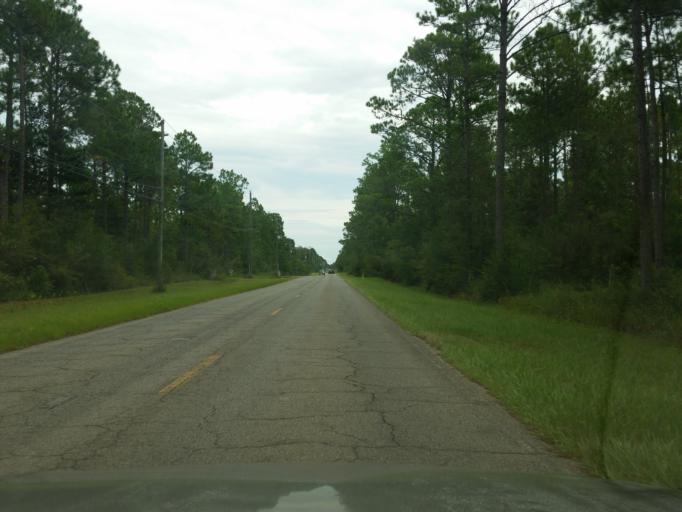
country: US
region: Florida
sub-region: Santa Rosa County
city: Pace
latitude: 30.5442
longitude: -87.0983
